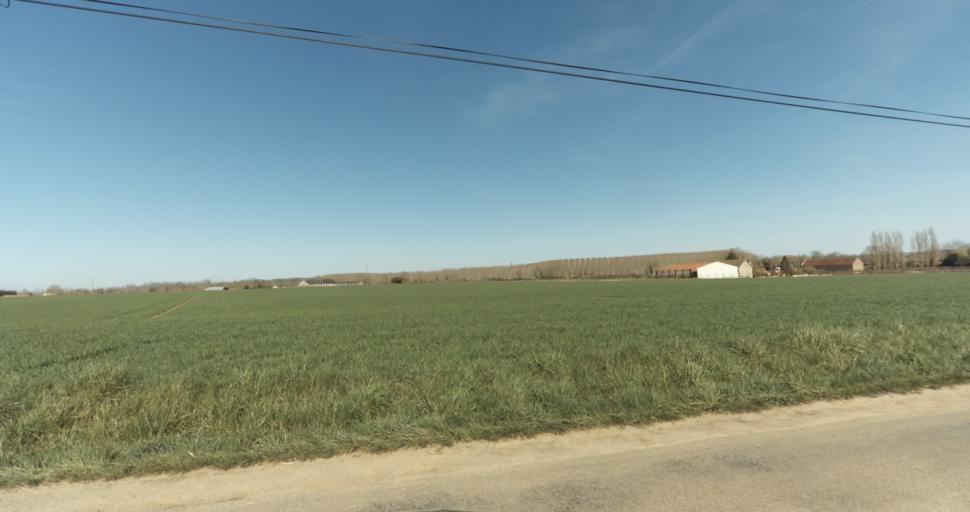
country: FR
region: Lower Normandy
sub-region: Departement du Calvados
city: Saint-Pierre-sur-Dives
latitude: 49.0526
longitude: -0.0549
